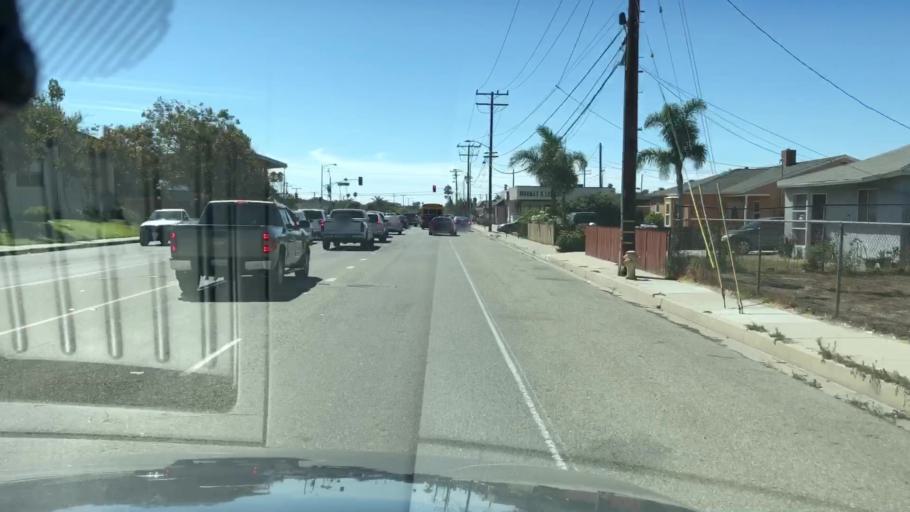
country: US
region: California
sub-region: Ventura County
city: Port Hueneme
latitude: 34.1611
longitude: -119.1760
